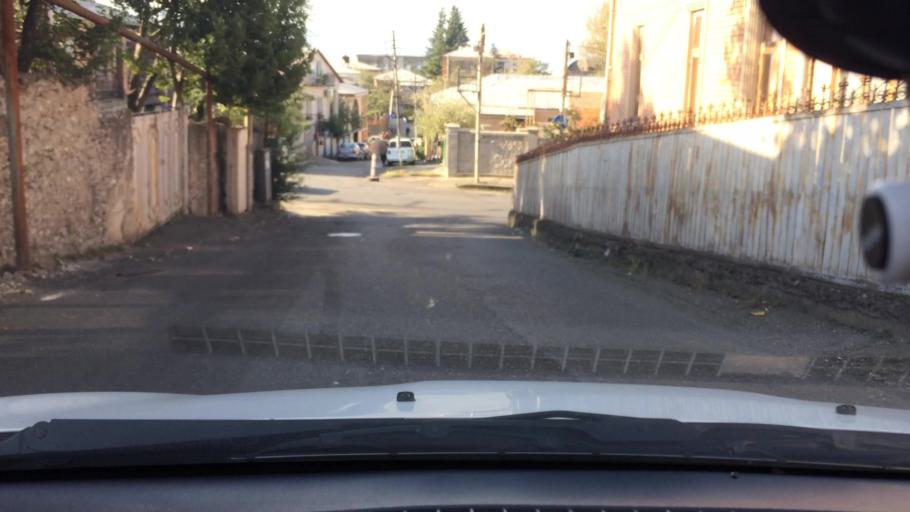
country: GE
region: Imereti
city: Kutaisi
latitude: 42.2710
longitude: 42.7105
